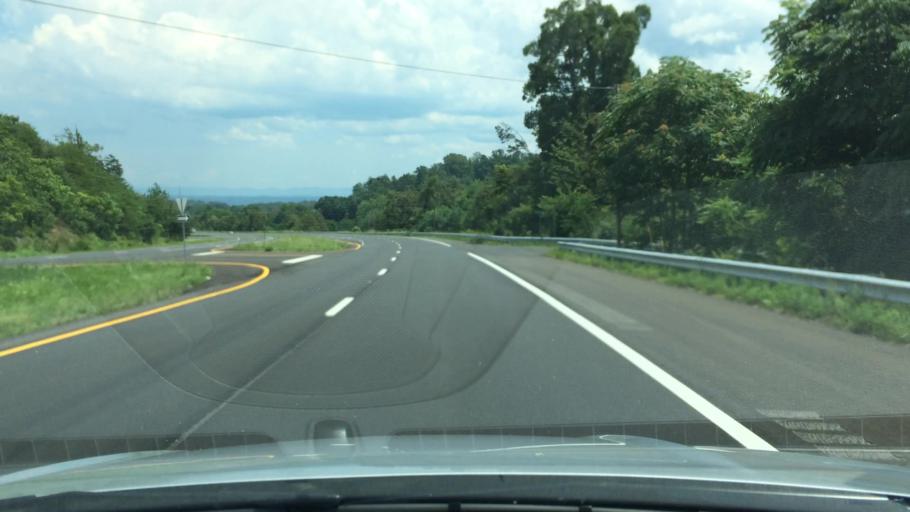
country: US
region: Tennessee
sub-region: Hamblen County
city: Morristown
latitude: 36.1860
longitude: -83.2578
